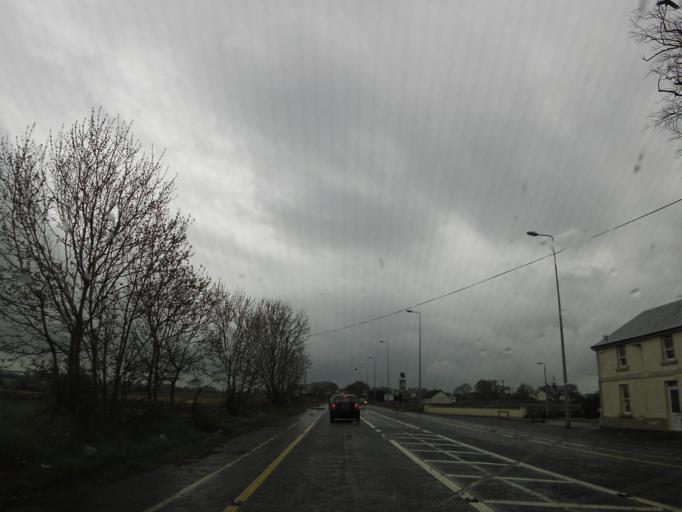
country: IE
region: Connaught
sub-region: County Galway
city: Claregalway
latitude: 53.3884
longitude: -8.9156
